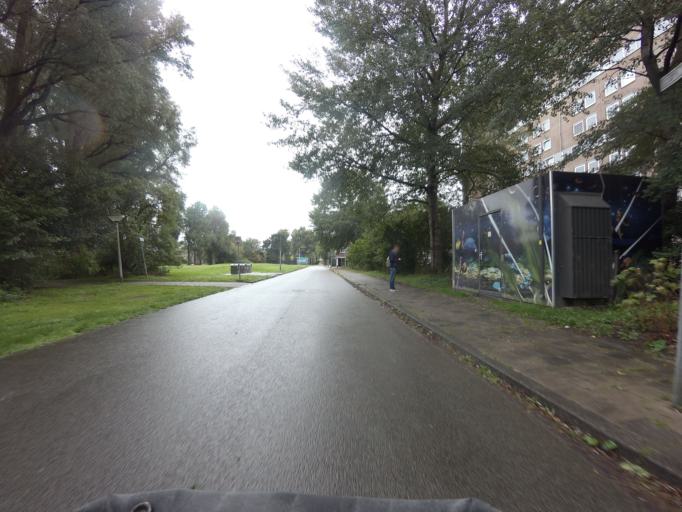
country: NL
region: Friesland
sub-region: Gemeente Leeuwarden
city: Bilgaard
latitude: 53.2179
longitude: 5.8054
